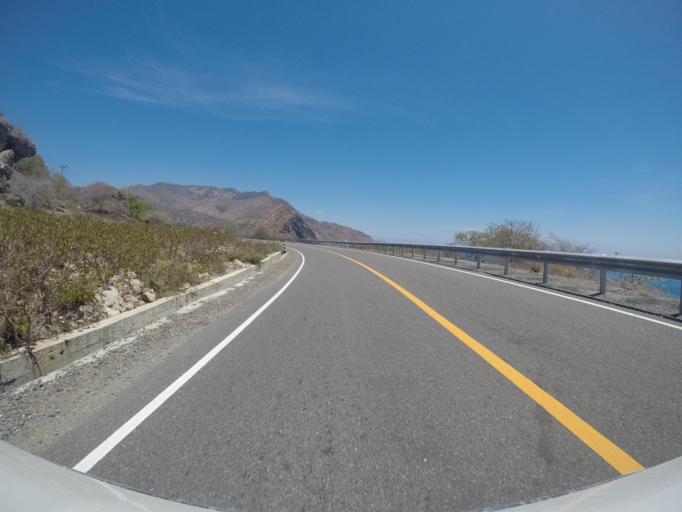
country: TL
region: Manatuto
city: Manatuto
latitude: -8.4851
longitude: 125.9792
